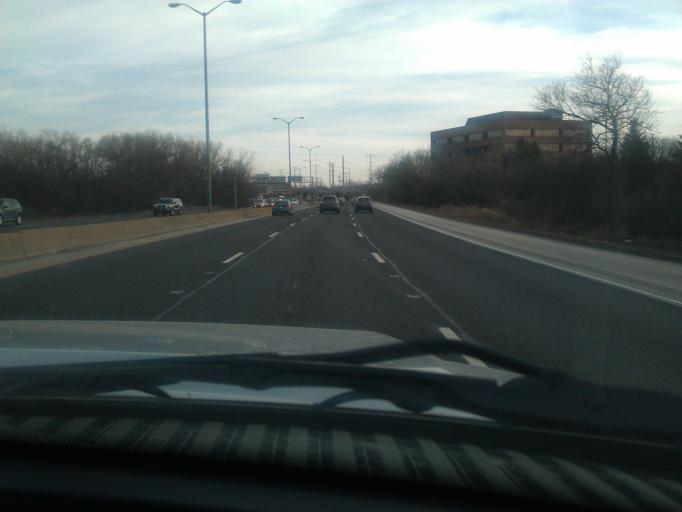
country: US
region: Illinois
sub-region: Cook County
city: Glencoe
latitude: 42.1320
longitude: -87.7855
